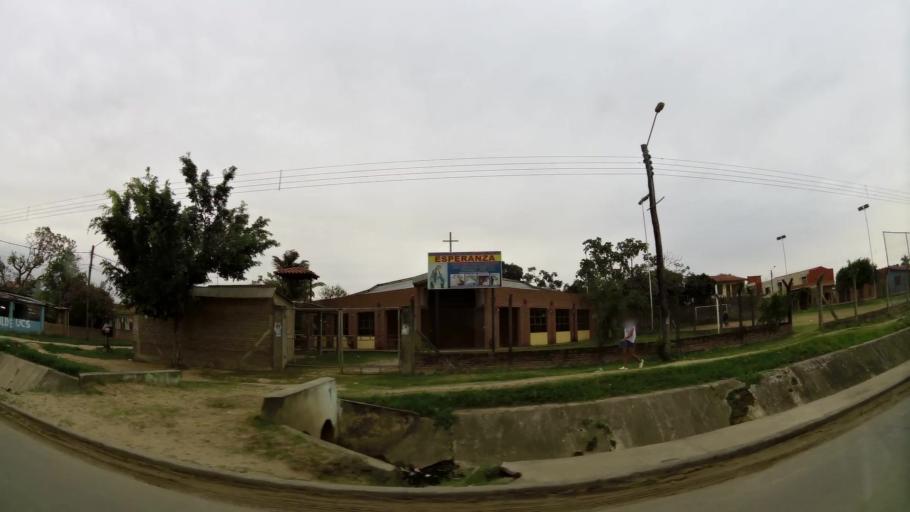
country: BO
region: Santa Cruz
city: Santa Cruz de la Sierra
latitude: -17.8562
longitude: -63.1654
